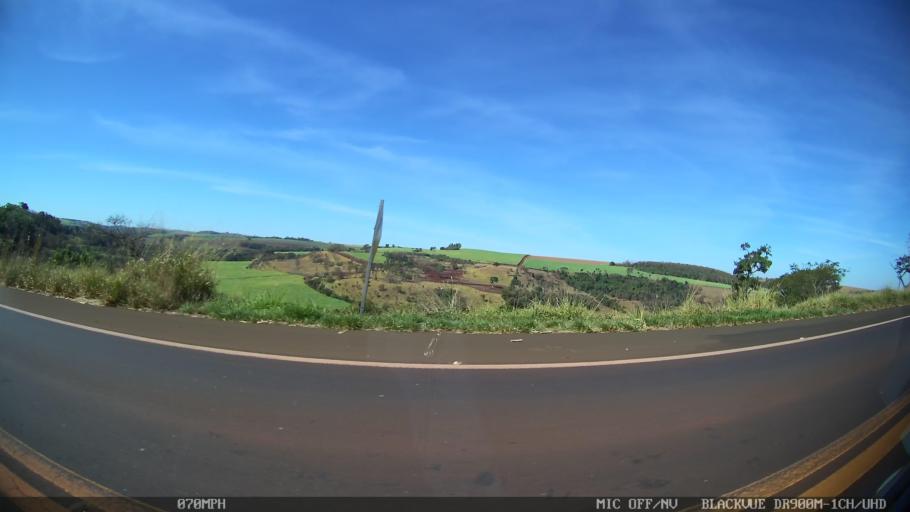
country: BR
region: Sao Paulo
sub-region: Sao Joaquim Da Barra
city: Sao Joaquim da Barra
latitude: -20.5591
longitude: -47.6827
